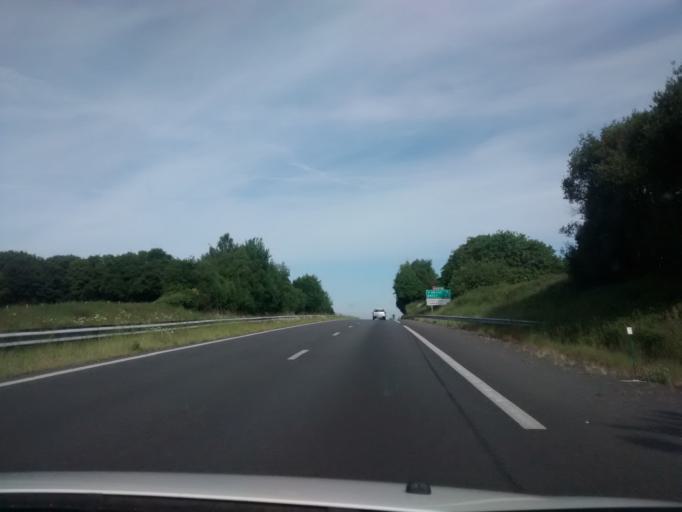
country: FR
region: Brittany
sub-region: Departement d'Ille-et-Vilaine
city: Montauban-de-Bretagne
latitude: 48.2128
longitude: -2.0871
